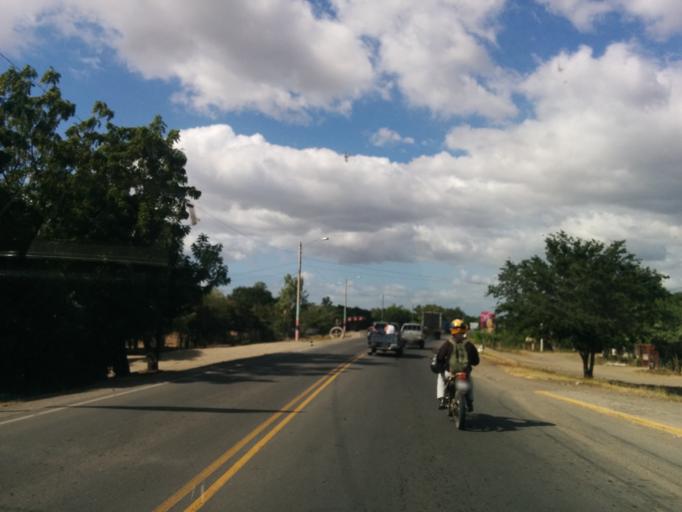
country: NI
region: Matagalpa
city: Ciudad Dario
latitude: 12.6657
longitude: -86.0872
